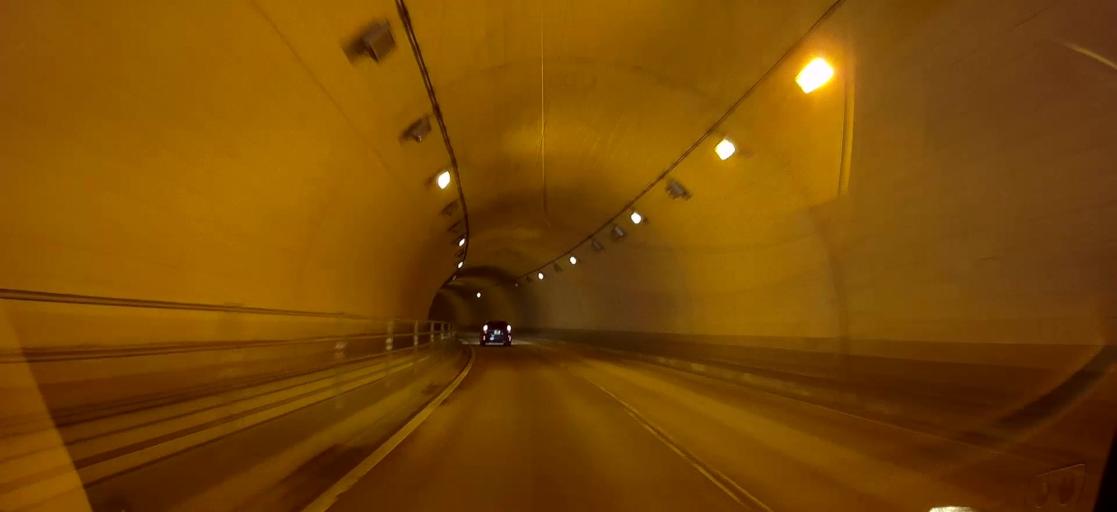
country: JP
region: Kumamoto
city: Hondo
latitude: 32.4403
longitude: 130.4053
